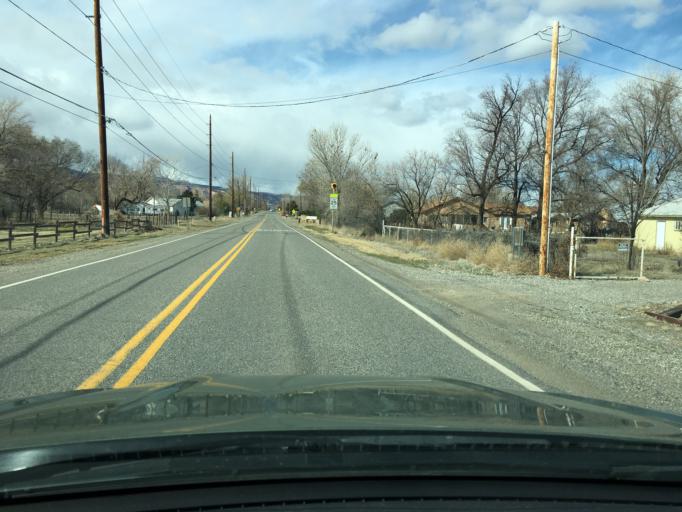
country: US
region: Colorado
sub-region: Mesa County
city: Redlands
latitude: 39.1209
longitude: -108.6122
